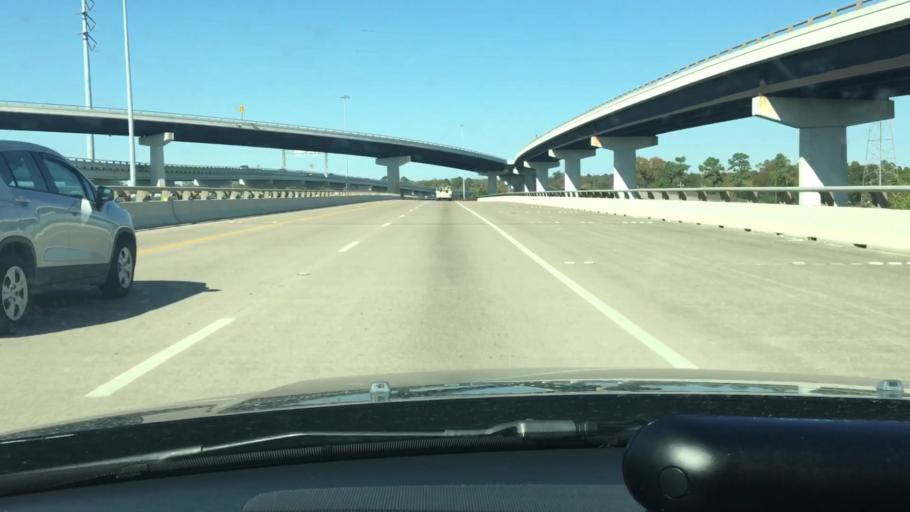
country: US
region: Texas
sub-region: Harris County
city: Cloverleaf
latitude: 29.7727
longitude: -95.1545
